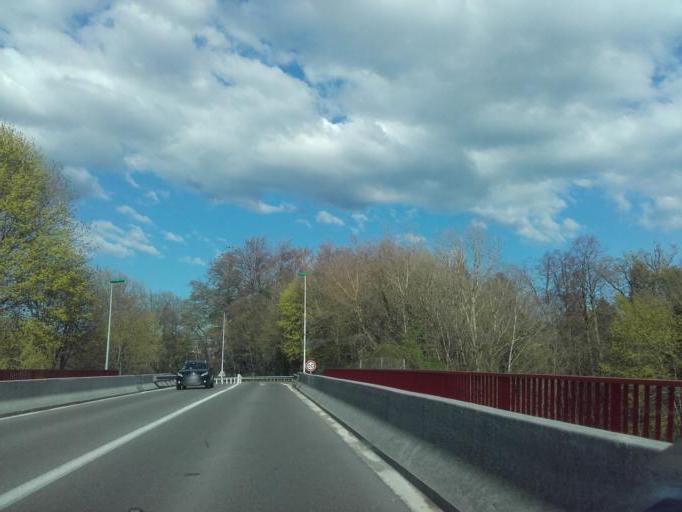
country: FR
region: Rhone-Alpes
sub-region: Departement de l'Isere
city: Ruy
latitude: 45.5823
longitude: 5.3033
